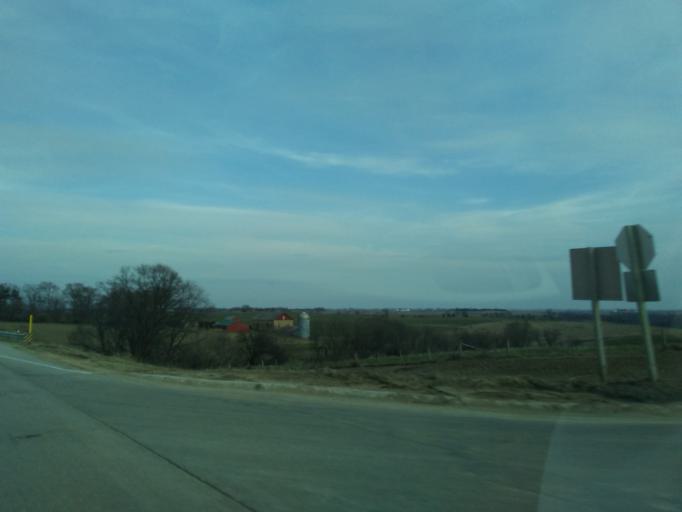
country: US
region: Wisconsin
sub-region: Iowa County
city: Barneveld
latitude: 43.0095
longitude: -89.9275
